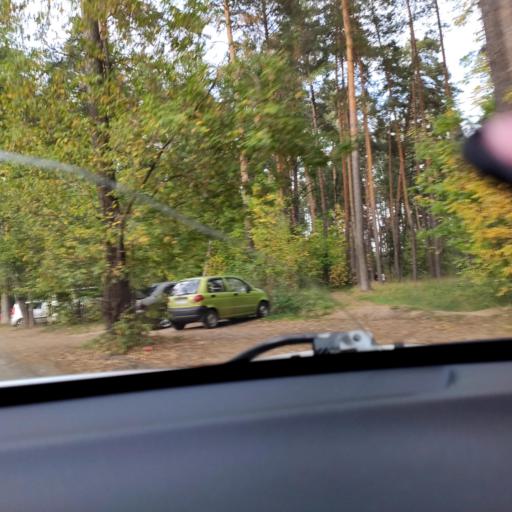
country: RU
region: Tatarstan
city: Staroye Arakchino
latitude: 55.8409
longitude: 48.9689
